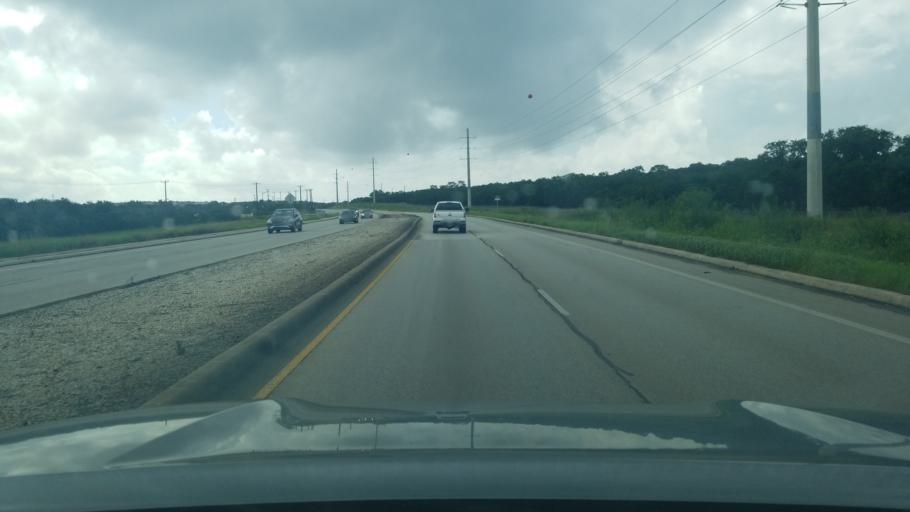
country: US
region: Texas
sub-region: Bexar County
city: Hollywood Park
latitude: 29.6553
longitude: -98.5210
